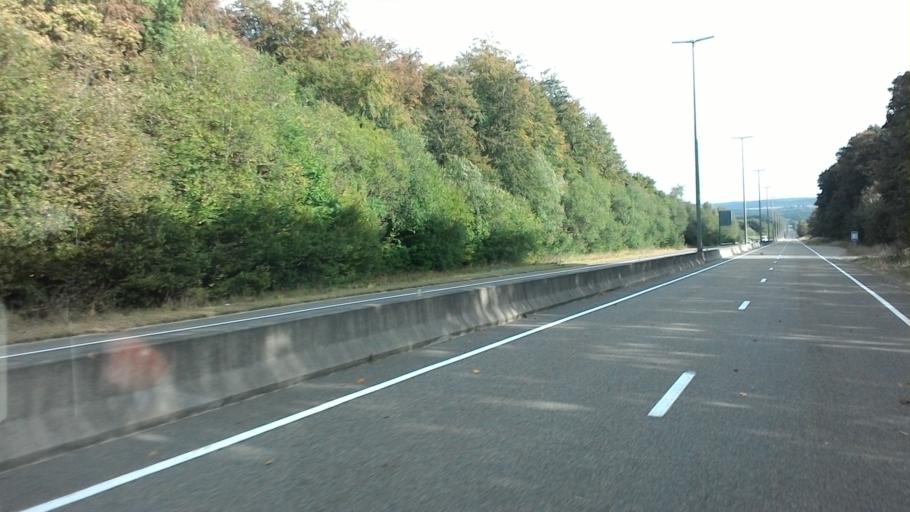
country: BE
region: Wallonia
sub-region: Province du Luxembourg
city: Attert
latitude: 49.7772
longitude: 5.7560
